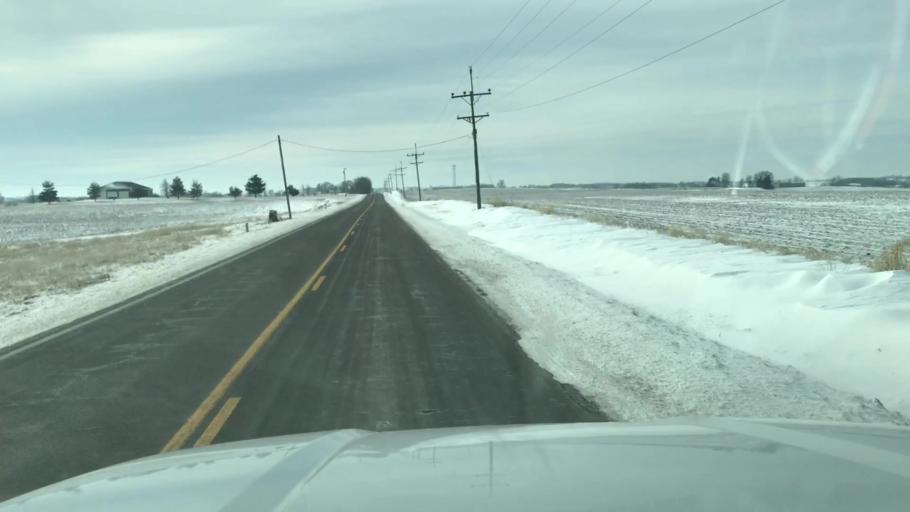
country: US
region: Missouri
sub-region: Holt County
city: Oregon
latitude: 40.0589
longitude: -95.1357
